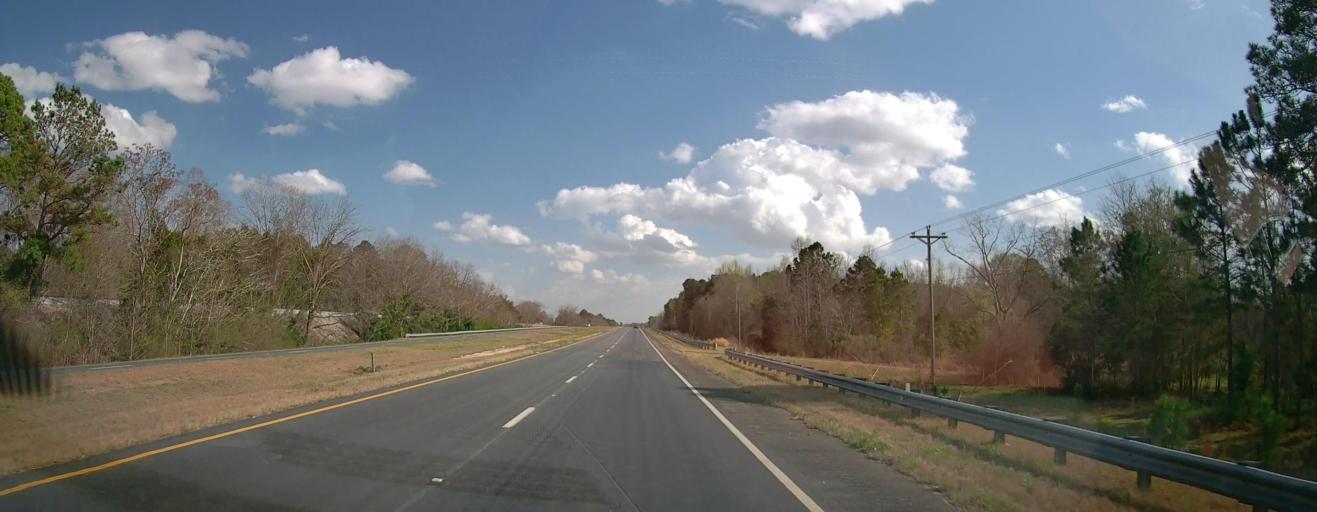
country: US
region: Georgia
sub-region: Dodge County
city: Eastman
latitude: 32.1400
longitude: -83.1312
